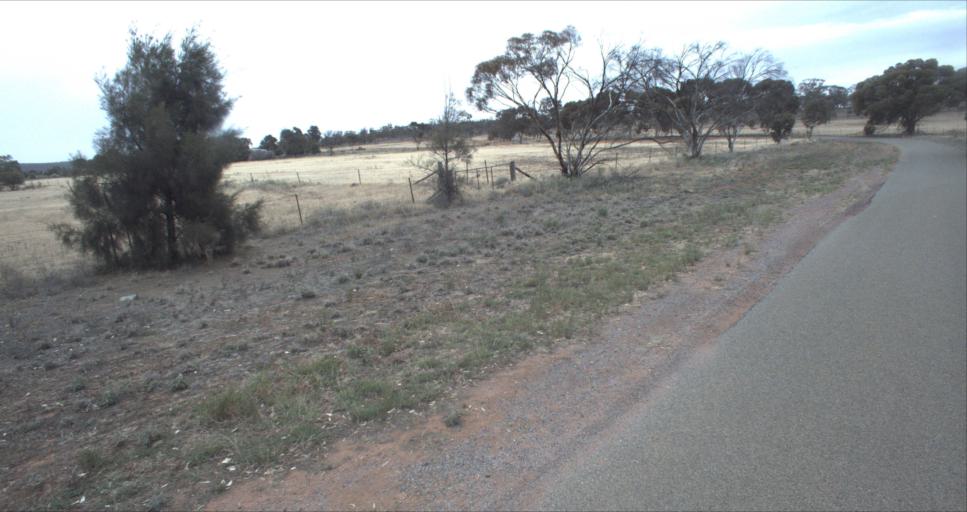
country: AU
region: New South Wales
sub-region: Leeton
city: Leeton
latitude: -34.4521
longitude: 146.3924
